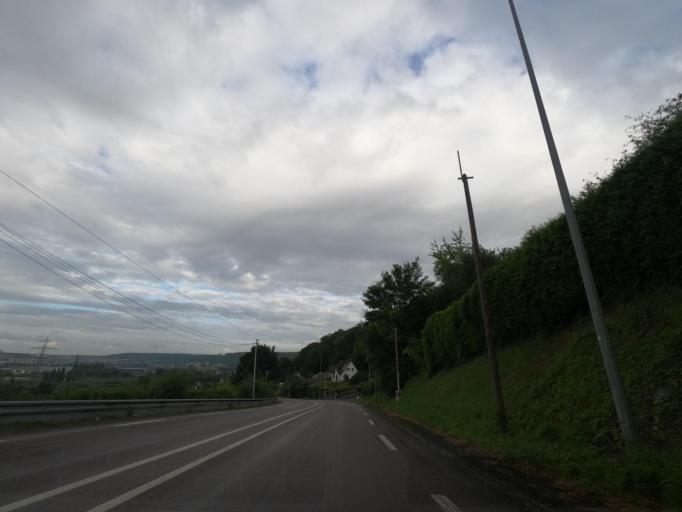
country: FR
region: Haute-Normandie
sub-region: Departement de la Seine-Maritime
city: Sahurs
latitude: 49.3409
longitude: 0.9603
